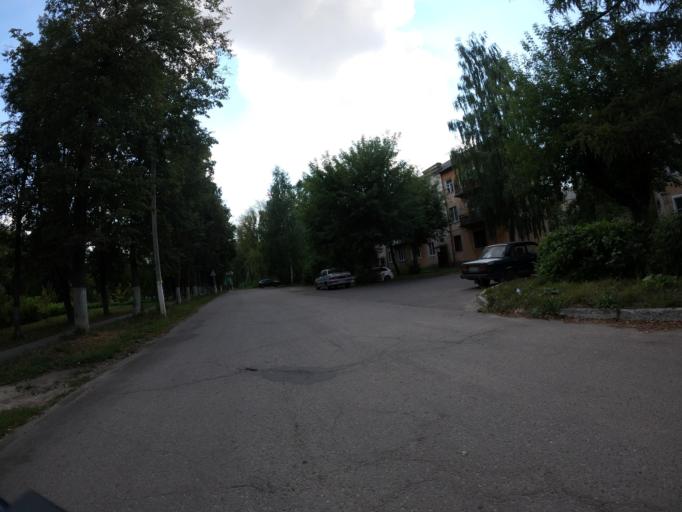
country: RU
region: Moskovskaya
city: Peski
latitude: 55.2699
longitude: 38.7361
